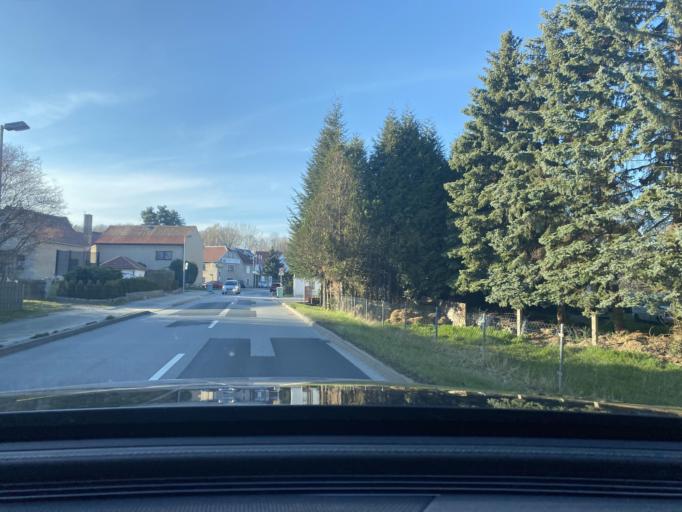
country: DE
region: Saxony
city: Grosspostwitz
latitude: 51.1048
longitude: 14.4456
